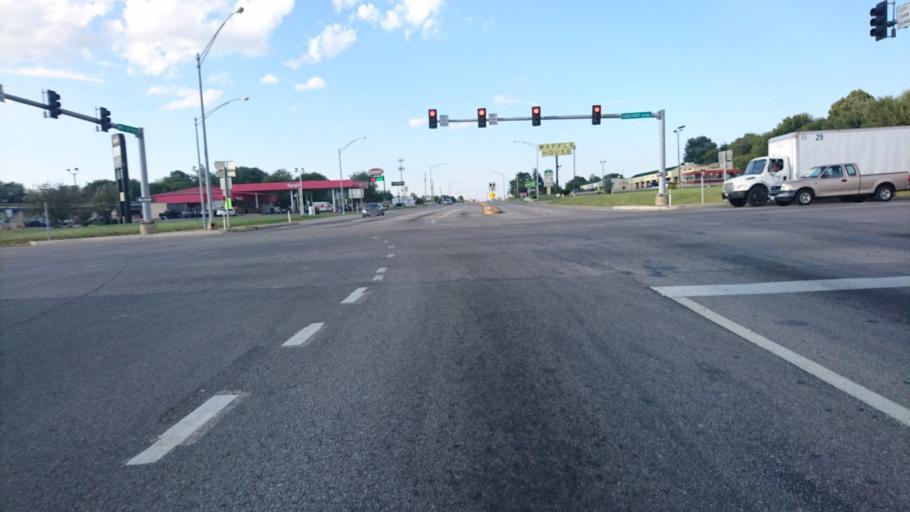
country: US
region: Missouri
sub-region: Greene County
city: Springfield
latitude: 37.2120
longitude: -93.3488
